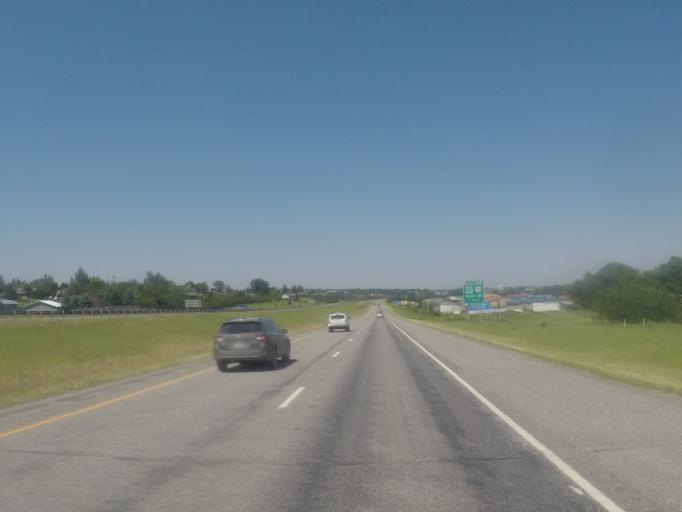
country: US
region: Montana
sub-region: Gallatin County
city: Bozeman
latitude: 45.6687
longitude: -110.9898
